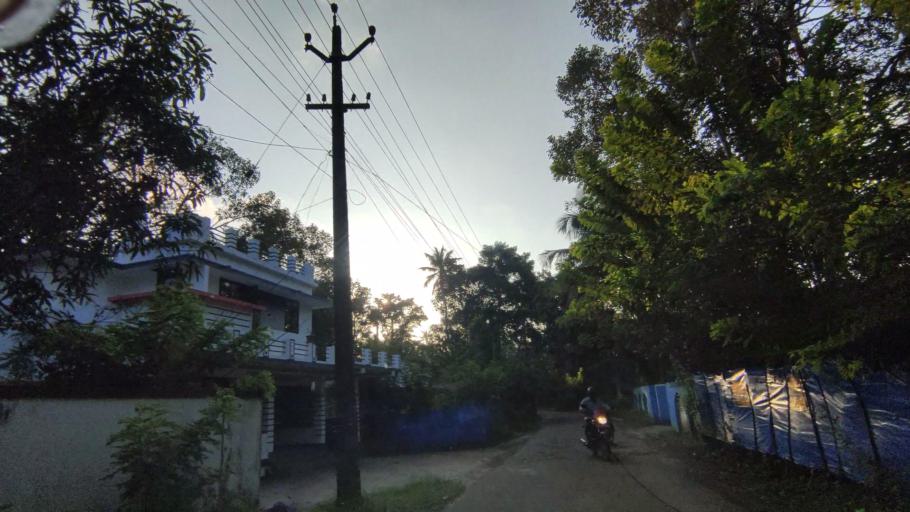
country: IN
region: Kerala
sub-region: Alappuzha
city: Shertallai
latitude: 9.6489
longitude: 76.3647
